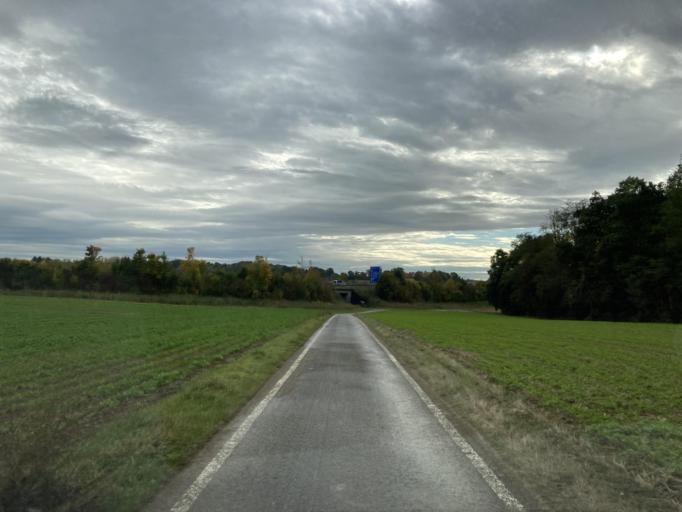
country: DE
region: Baden-Wuerttemberg
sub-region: Regierungsbezirk Stuttgart
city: Bondorf
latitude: 48.5115
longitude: 8.8542
